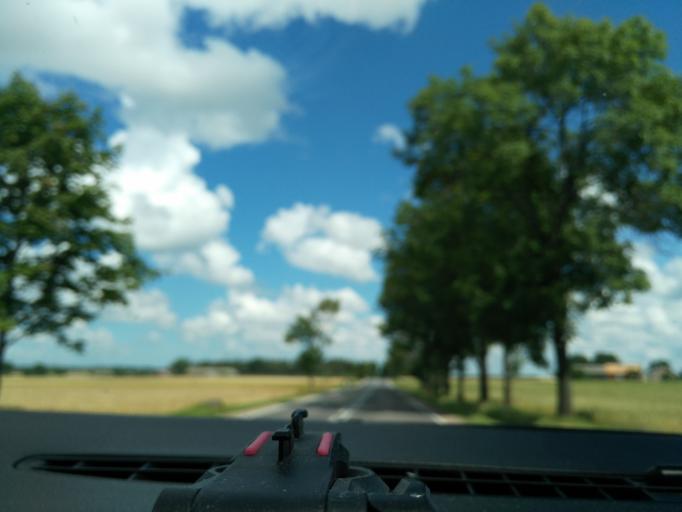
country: PL
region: Masovian Voivodeship
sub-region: Powiat losicki
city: Sarnaki
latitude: 52.2781
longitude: 22.8324
